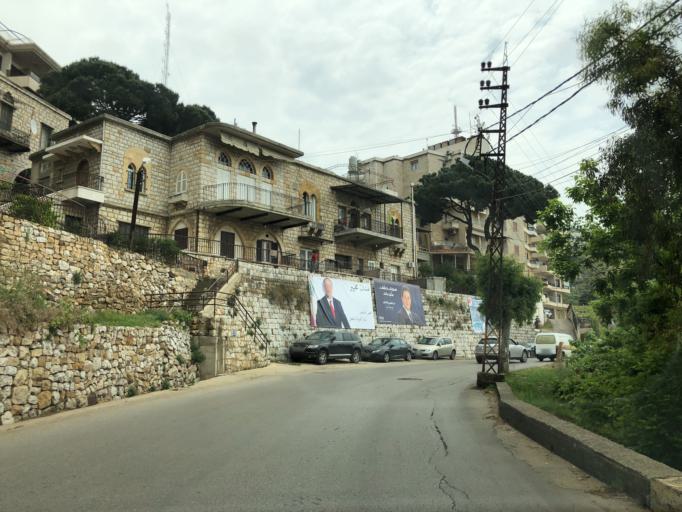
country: LB
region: Mont-Liban
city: Jdaidet el Matn
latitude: 33.8645
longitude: 35.6029
